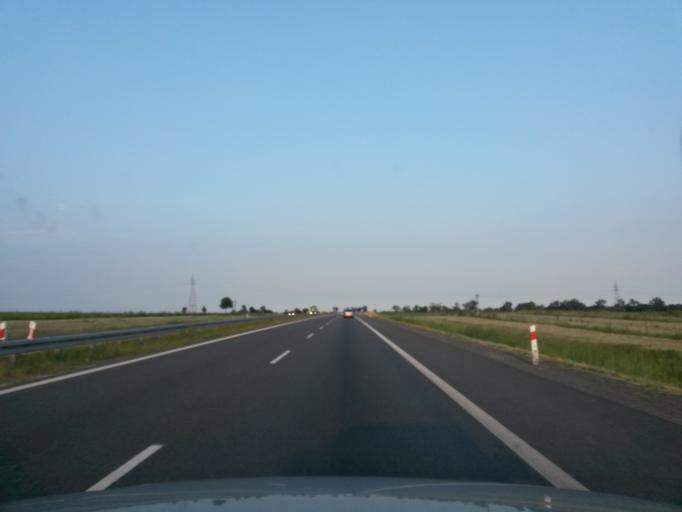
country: PL
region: Lower Silesian Voivodeship
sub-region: Powiat olesnicki
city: Sycow
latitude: 51.2982
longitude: 17.6586
